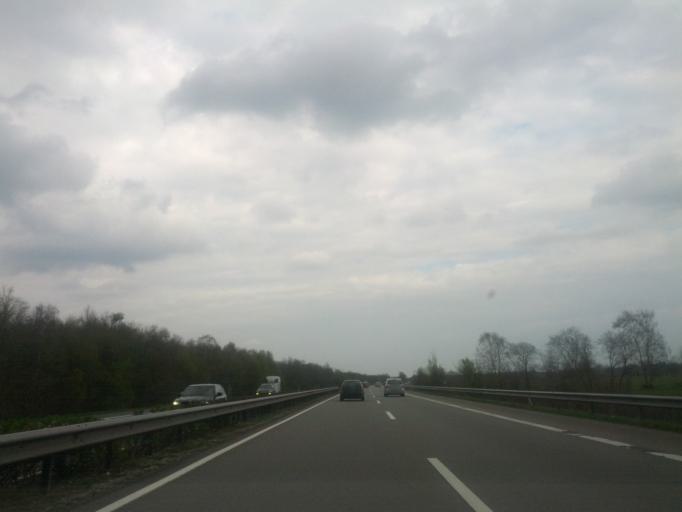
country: DE
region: Lower Saxony
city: Apen
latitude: 53.2834
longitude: 7.8329
